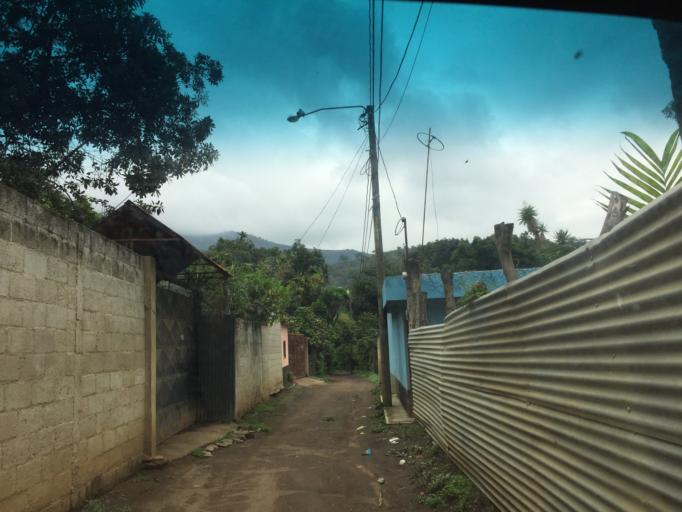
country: GT
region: Sacatepequez
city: Magdalena Milpas Altas
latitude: 14.5110
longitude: -90.6545
